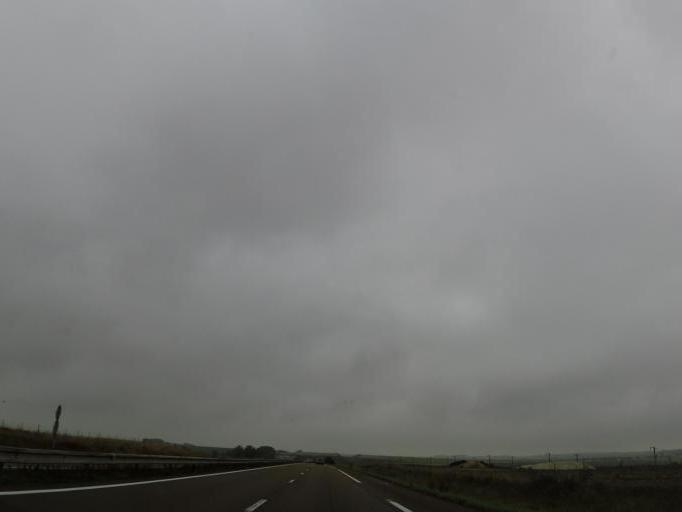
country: FR
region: Champagne-Ardenne
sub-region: Departement de la Marne
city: Verzy
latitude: 49.1556
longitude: 4.1982
